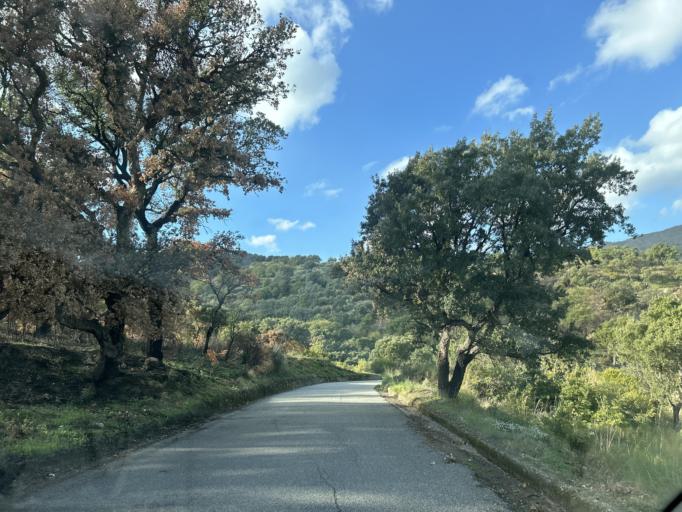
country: IT
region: Calabria
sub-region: Provincia di Catanzaro
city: Montepaone
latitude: 38.7169
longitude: 16.5149
